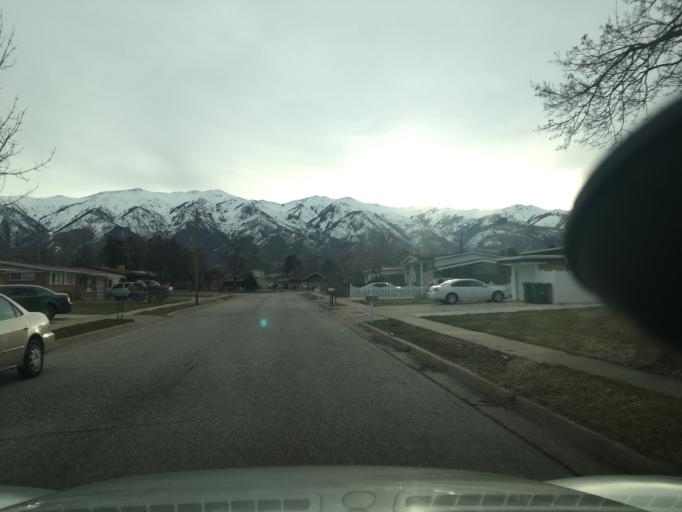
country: US
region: Utah
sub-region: Davis County
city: Layton
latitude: 41.0738
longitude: -111.9630
